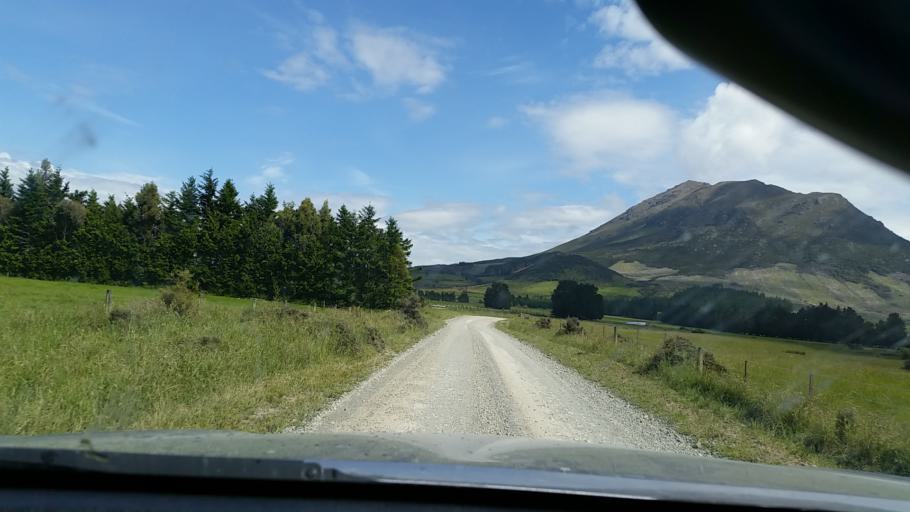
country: NZ
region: Otago
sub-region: Queenstown-Lakes District
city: Kingston
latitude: -45.6235
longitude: 168.2682
